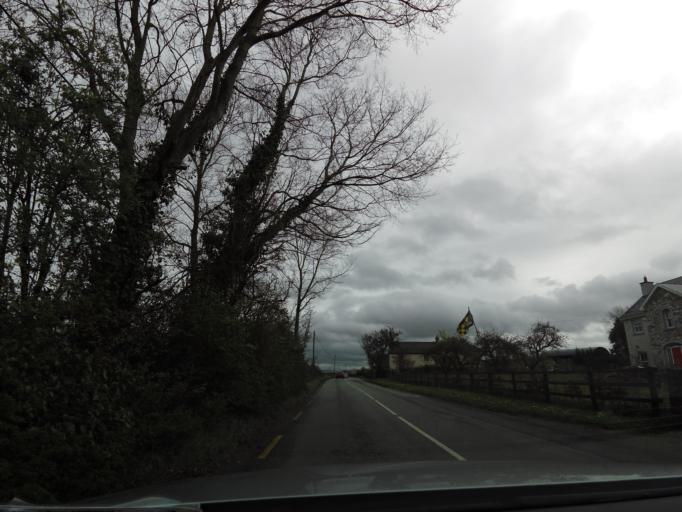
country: IE
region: Leinster
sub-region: Kilkenny
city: Ballyragget
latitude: 52.7306
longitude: -7.3877
